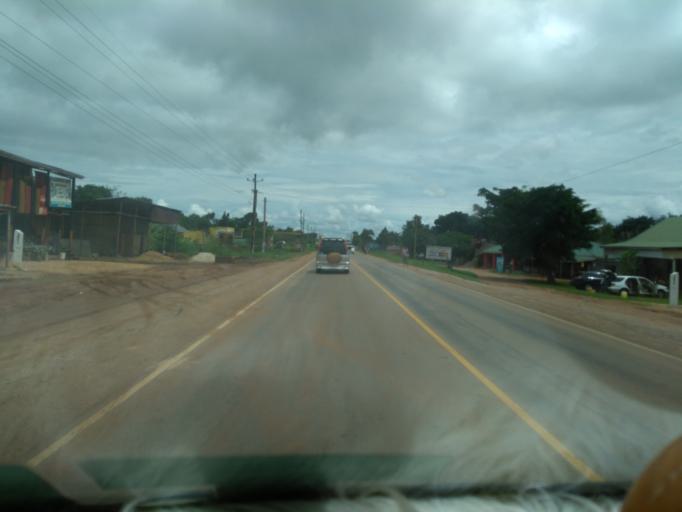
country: UG
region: Central Region
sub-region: Butambala District
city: Gombe
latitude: -0.0001
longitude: 32.0399
